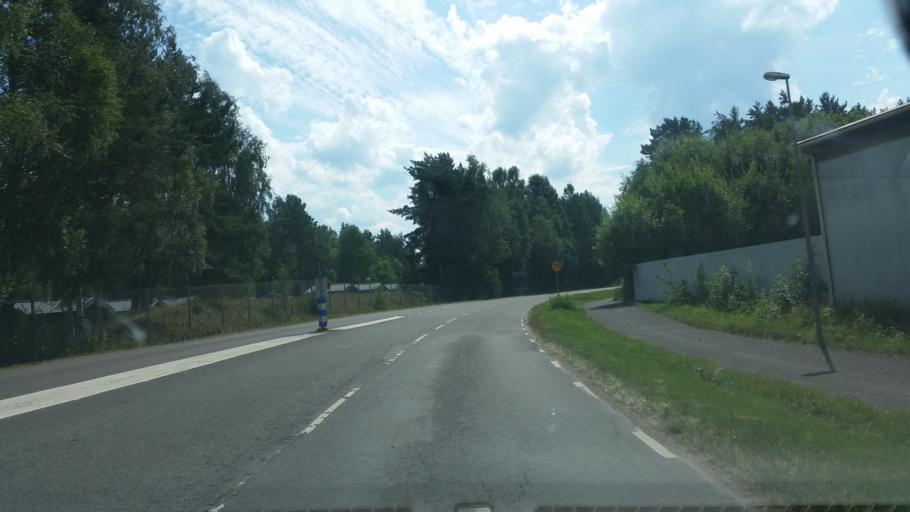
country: SE
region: Vaestra Goetaland
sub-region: Skara Kommun
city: Axvall
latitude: 58.4099
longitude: 13.5559
